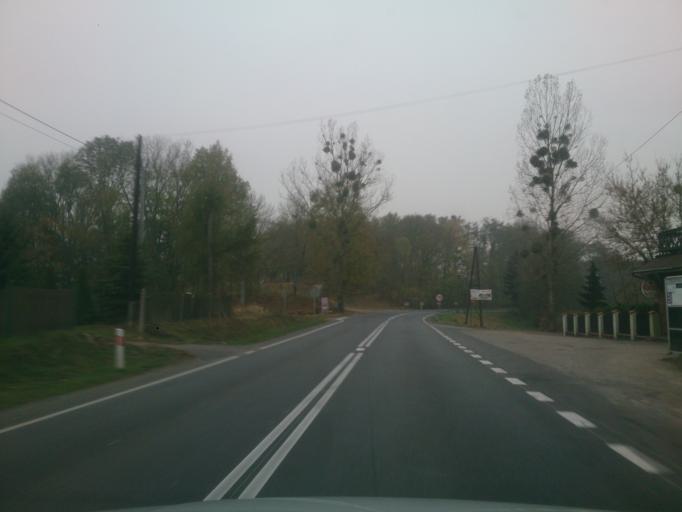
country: PL
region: Kujawsko-Pomorskie
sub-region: Powiat brodnicki
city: Bobrowo
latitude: 53.2442
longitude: 19.2997
